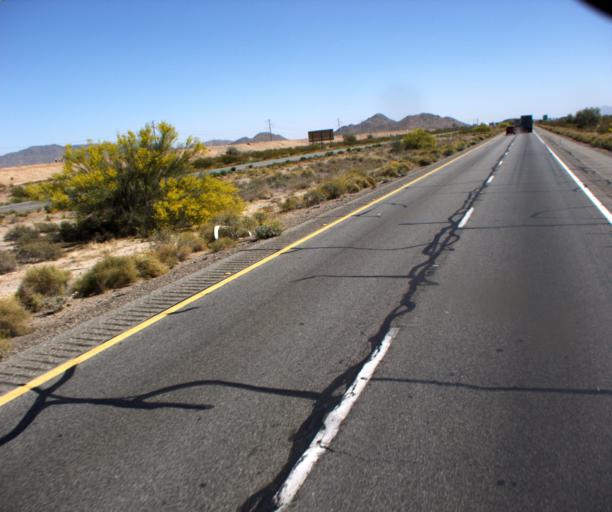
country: US
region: Arizona
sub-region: Maricopa County
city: Buckeye
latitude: 33.4367
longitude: -112.6667
